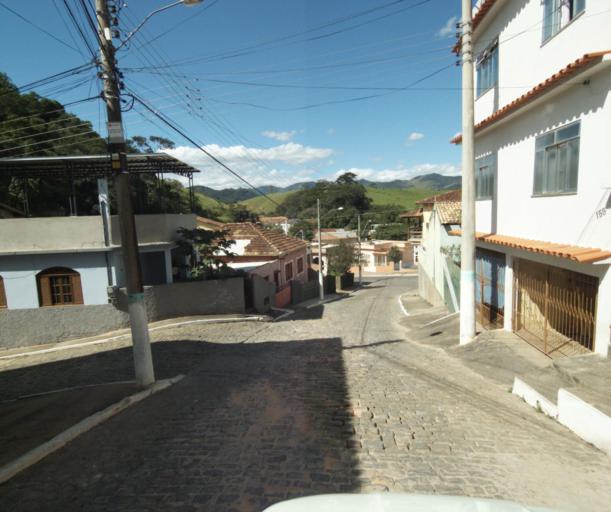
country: BR
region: Espirito Santo
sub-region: Sao Jose Do Calcado
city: Sao Jose do Calcado
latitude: -21.0251
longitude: -41.6533
